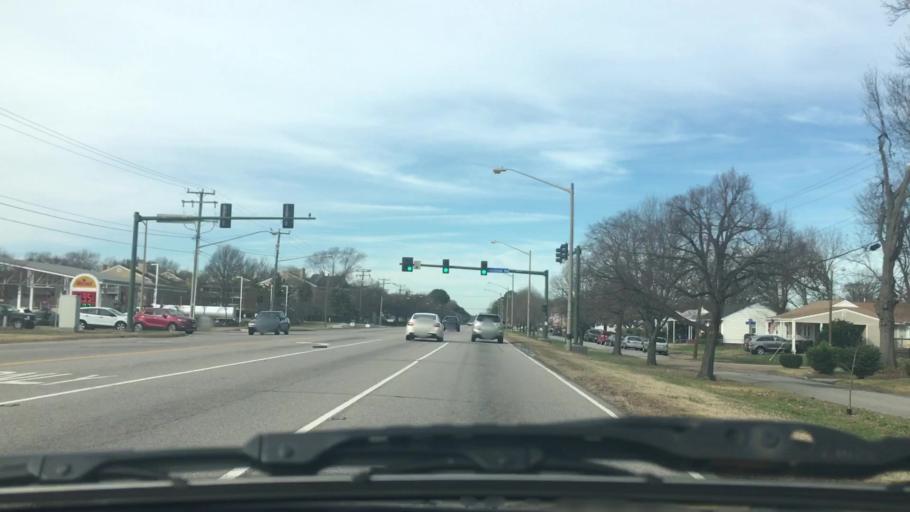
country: US
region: Virginia
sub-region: City of Norfolk
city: Norfolk
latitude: 36.8966
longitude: -76.2248
